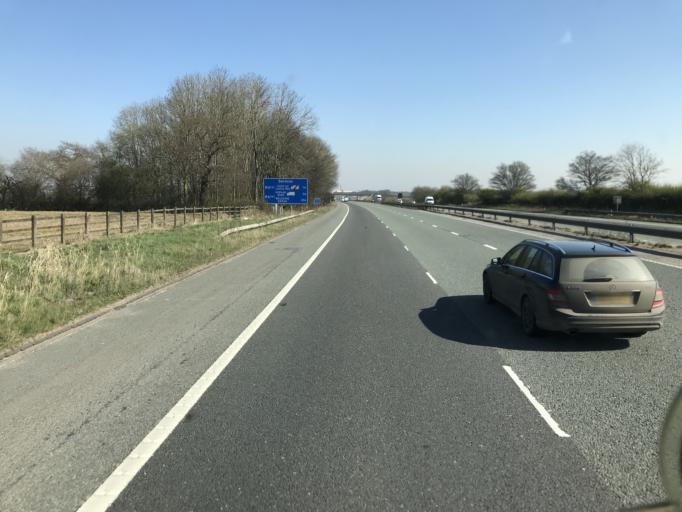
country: GB
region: England
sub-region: Warrington
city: Stretton
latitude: 53.3375
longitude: -2.5595
